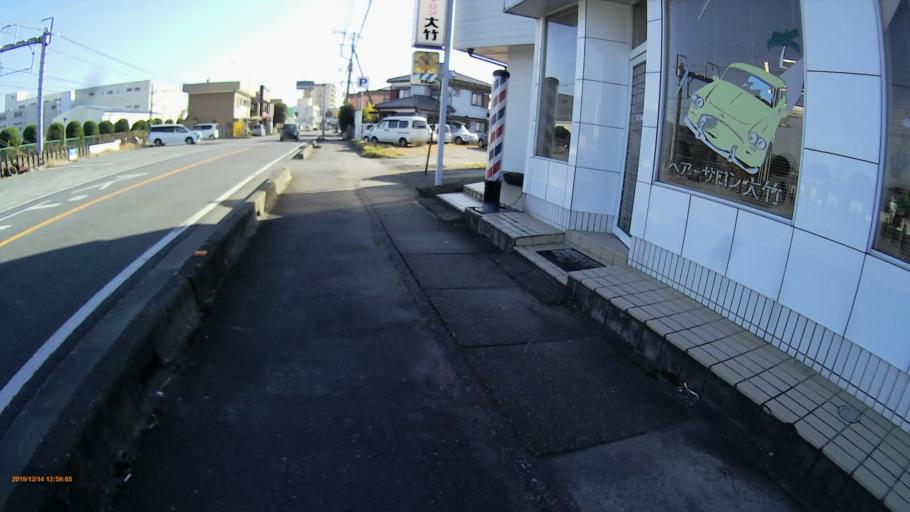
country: JP
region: Saitama
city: Fukiage-fujimi
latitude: 36.0988
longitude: 139.4608
